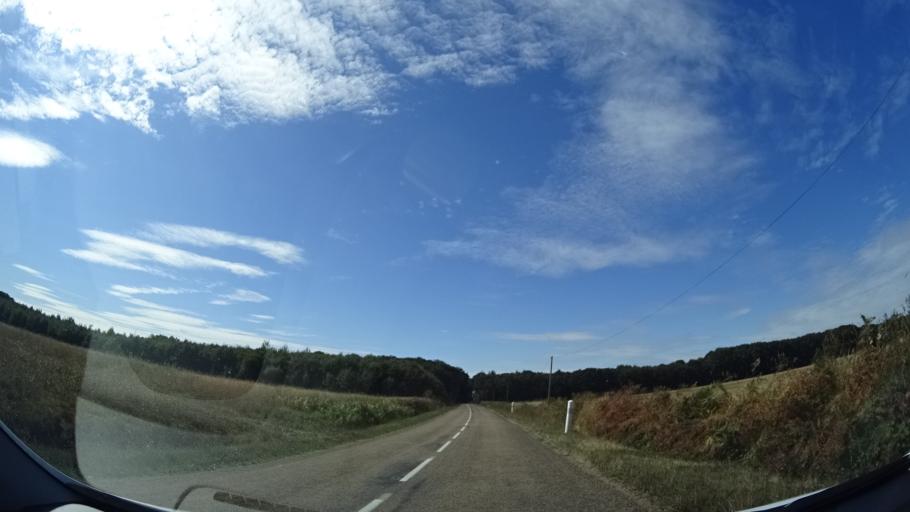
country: FR
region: Bourgogne
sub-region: Departement de l'Yonne
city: Aillant-sur-Tholon
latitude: 47.9211
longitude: 3.3036
